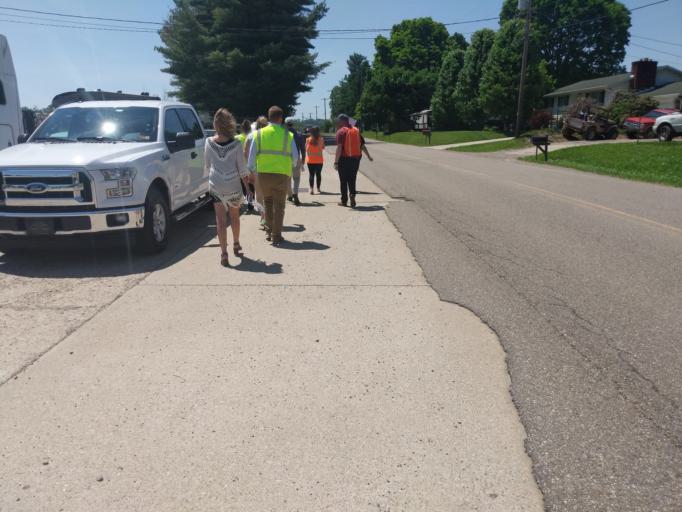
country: US
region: Ohio
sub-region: Washington County
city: Reno
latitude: 39.3919
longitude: -81.4001
